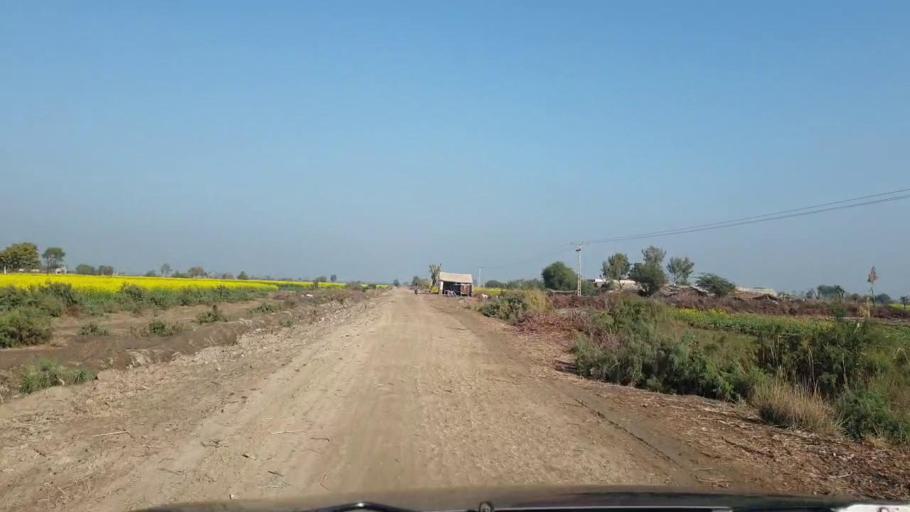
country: PK
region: Sindh
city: Sinjhoro
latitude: 26.0416
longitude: 68.7887
